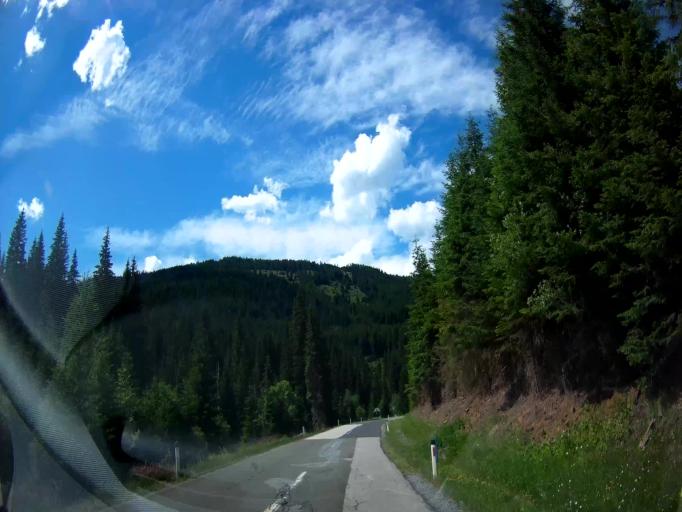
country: AT
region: Styria
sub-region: Politischer Bezirk Murau
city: Stadl an der Mur
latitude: 46.9768
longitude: 14.0072
